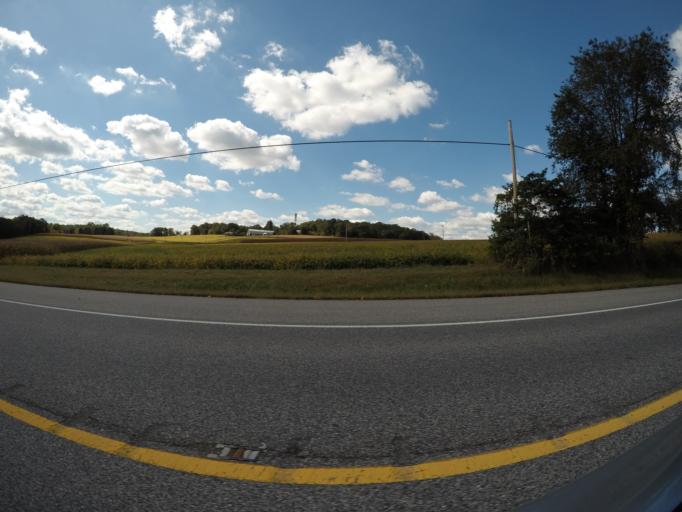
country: US
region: Pennsylvania
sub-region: York County
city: Susquehanna Trails
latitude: 39.6665
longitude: -76.2824
